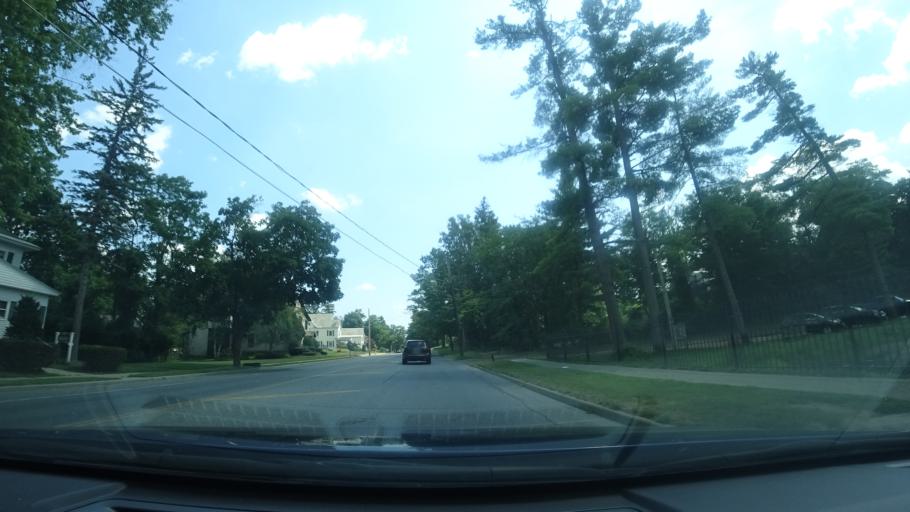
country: US
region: New York
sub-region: Warren County
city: Glens Falls
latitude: 43.3200
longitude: -73.6586
